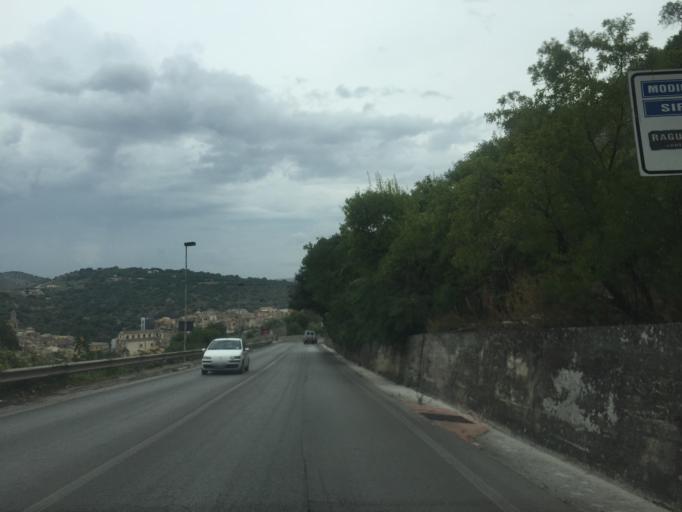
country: IT
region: Sicily
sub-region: Ragusa
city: Ragusa
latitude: 36.9224
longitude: 14.7346
